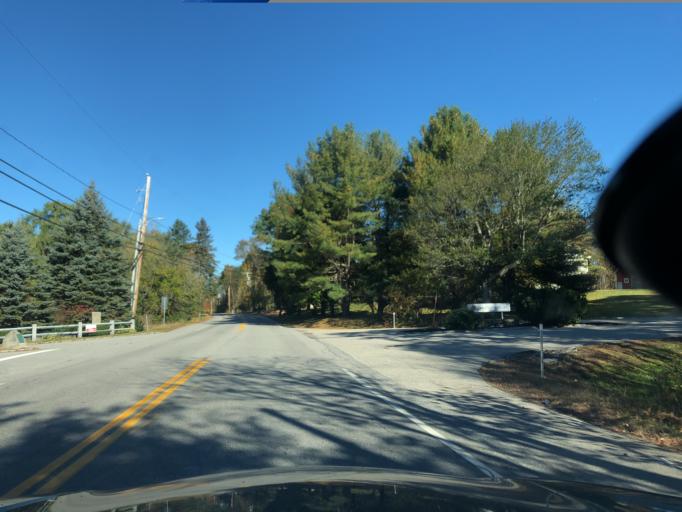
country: US
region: New Hampshire
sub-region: Rockingham County
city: Exeter
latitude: 43.0233
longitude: -70.9432
